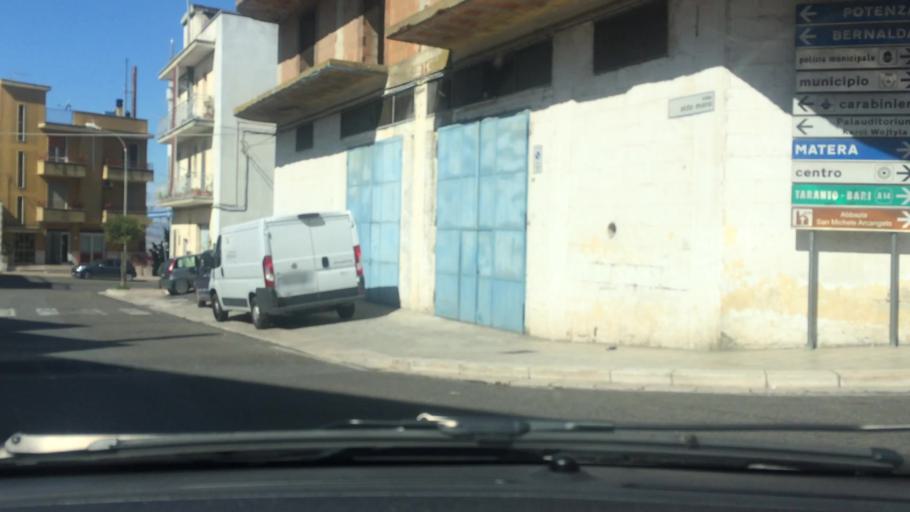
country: IT
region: Basilicate
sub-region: Provincia di Matera
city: Montescaglioso
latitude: 40.5495
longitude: 16.6663
